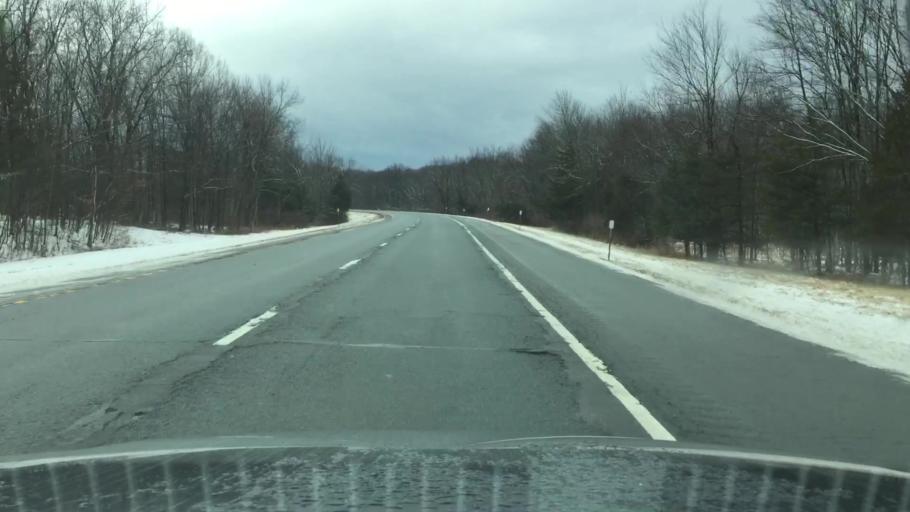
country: US
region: New York
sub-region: Orange County
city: Otisville
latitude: 41.3910
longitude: -74.5647
